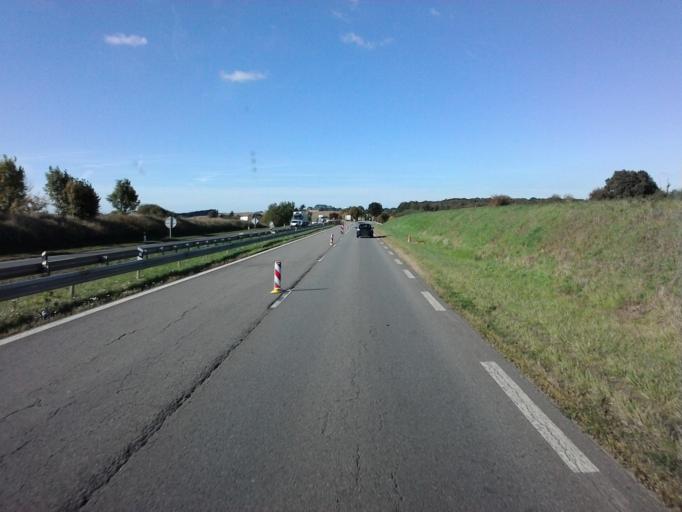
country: FR
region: Lorraine
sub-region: Departement de Meurthe-et-Moselle
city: Haucourt-Moulaine
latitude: 49.4879
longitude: 5.8135
